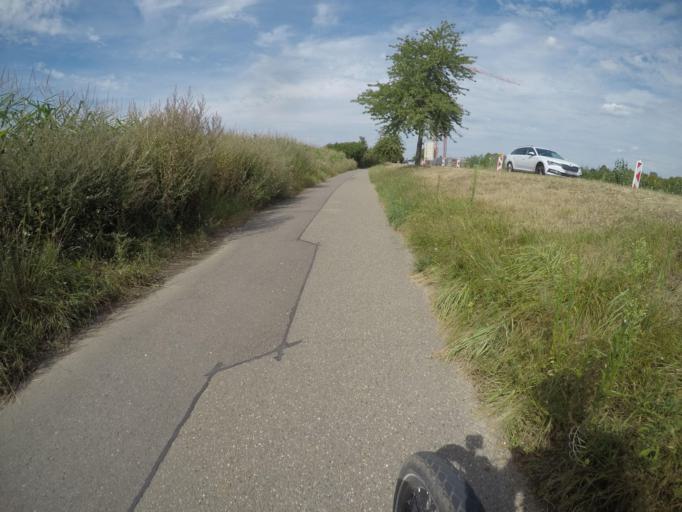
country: DE
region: Baden-Wuerttemberg
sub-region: Karlsruhe Region
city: Bruhl
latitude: 49.3884
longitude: 8.5279
